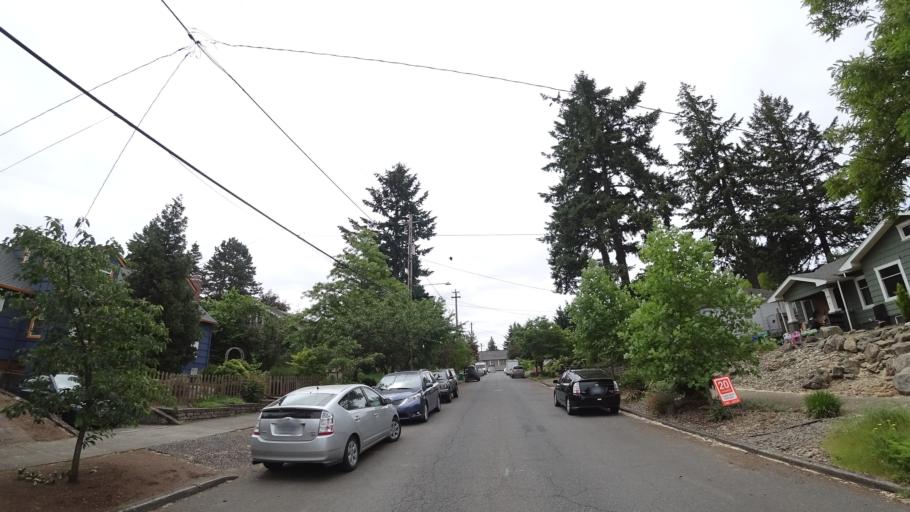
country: US
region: Oregon
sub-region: Multnomah County
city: Portland
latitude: 45.5640
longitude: -122.6382
